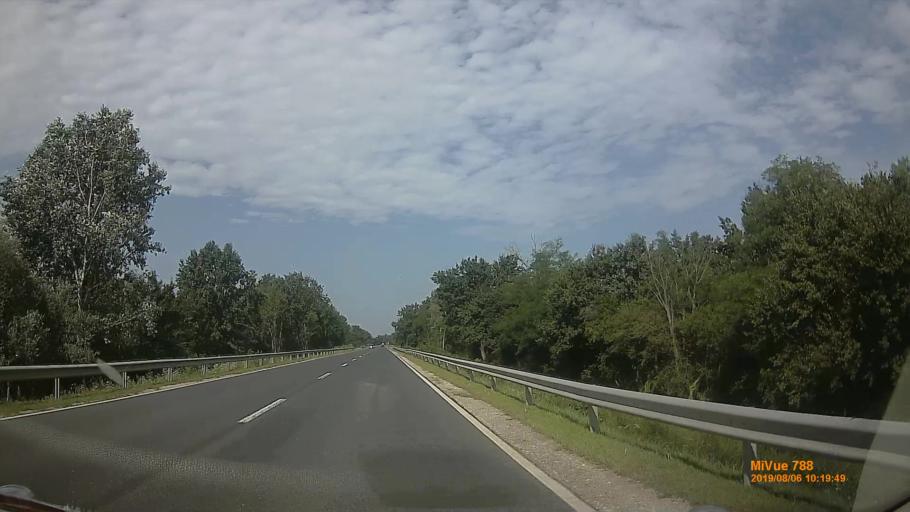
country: HU
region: Vas
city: Vasvar
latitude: 47.0587
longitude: 16.7679
